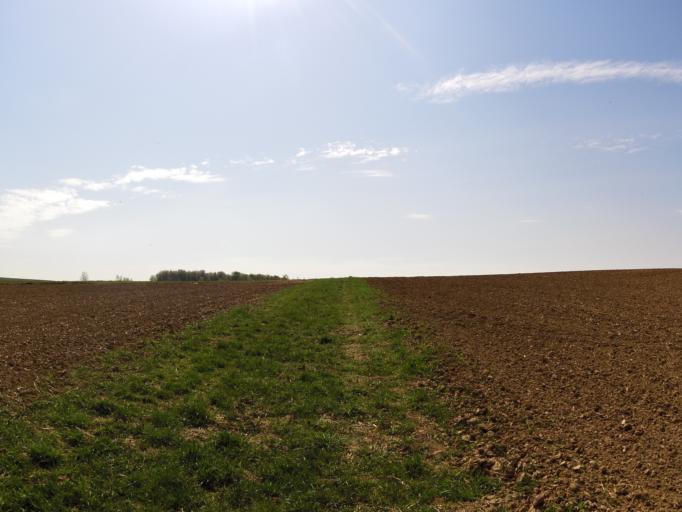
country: DE
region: Bavaria
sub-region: Regierungsbezirk Unterfranken
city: Giebelstadt
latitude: 49.6916
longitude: 9.9598
